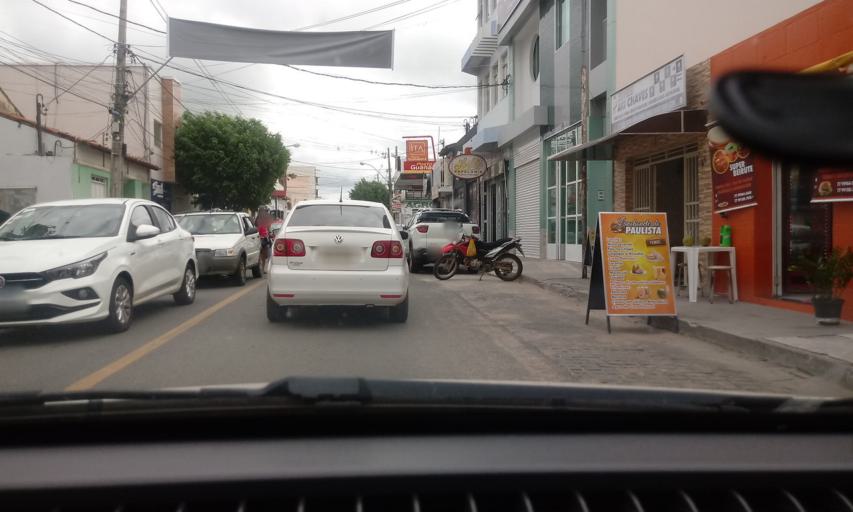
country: BR
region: Bahia
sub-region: Guanambi
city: Guanambi
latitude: -14.2217
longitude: -42.7800
